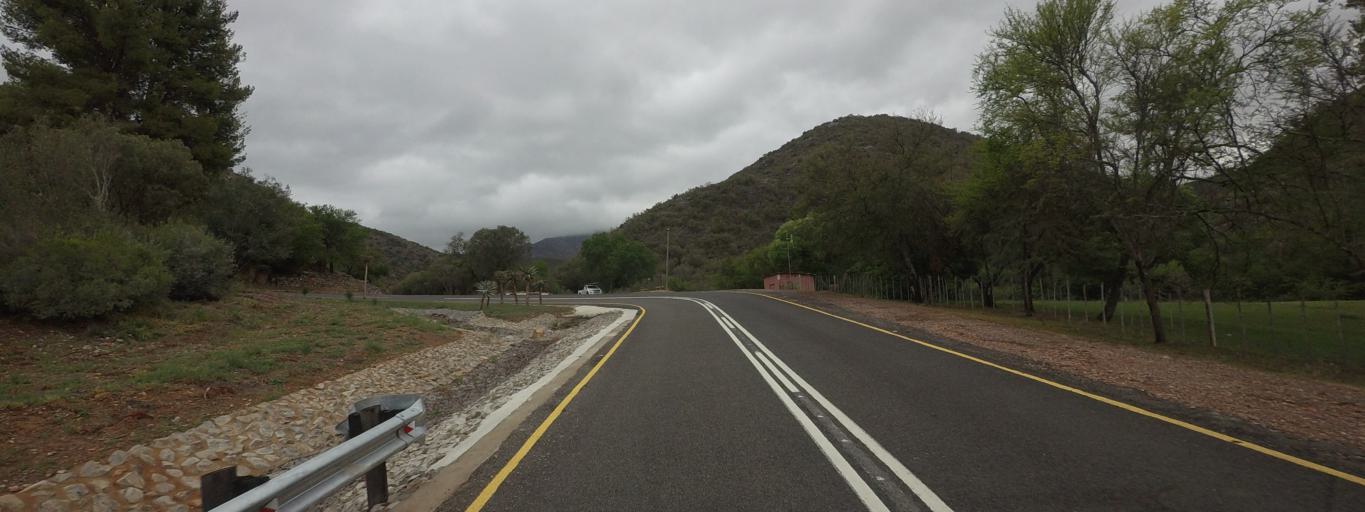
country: ZA
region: Western Cape
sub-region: Eden District Municipality
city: Oudtshoorn
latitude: -33.3937
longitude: 22.2158
